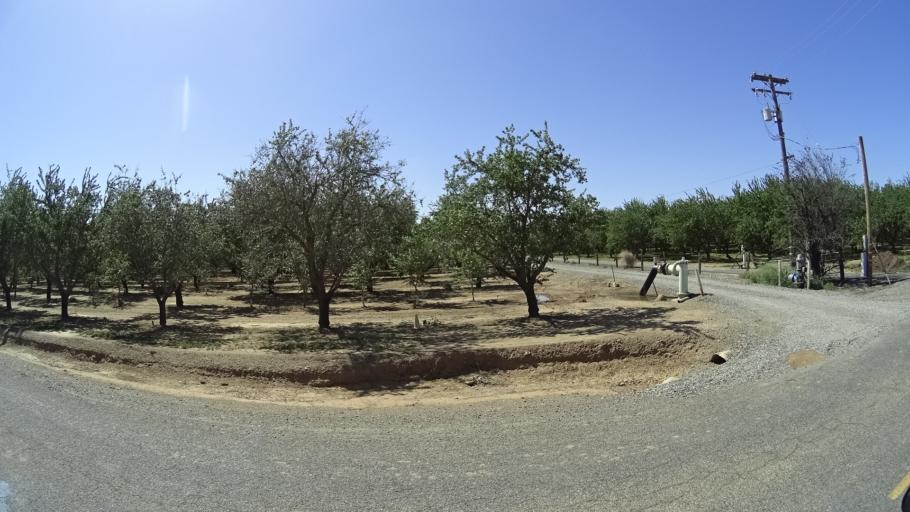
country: US
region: California
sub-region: Glenn County
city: Orland
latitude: 39.7111
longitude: -122.1916
